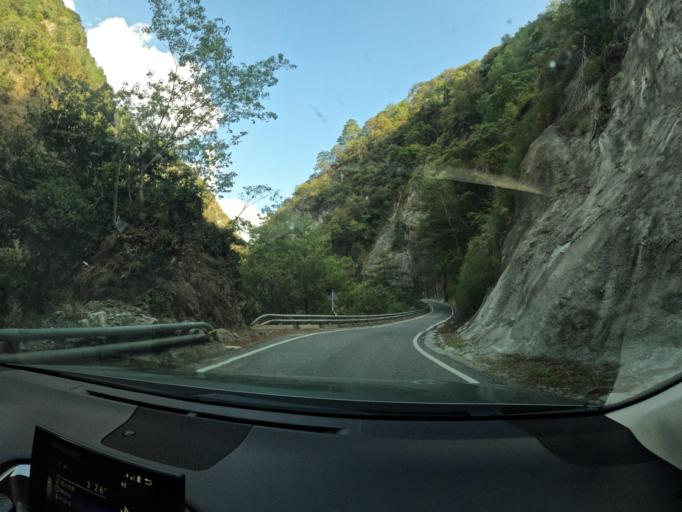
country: TW
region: Taiwan
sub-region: Taitung
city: Taitung
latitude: 23.1748
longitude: 121.0303
